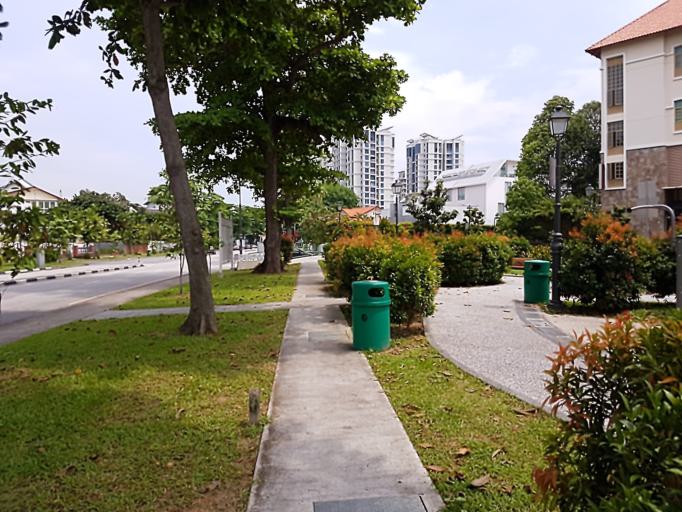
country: SG
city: Singapore
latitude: 1.3096
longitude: 103.8996
